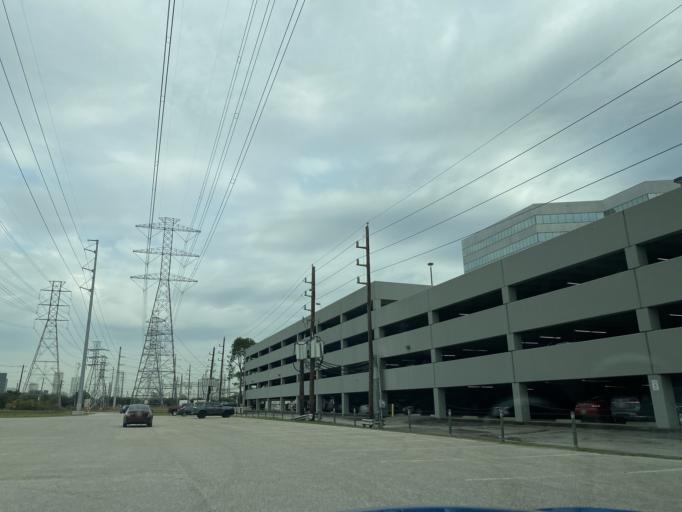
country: US
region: Texas
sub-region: Harris County
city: Bellaire
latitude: 29.7259
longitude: -95.4560
